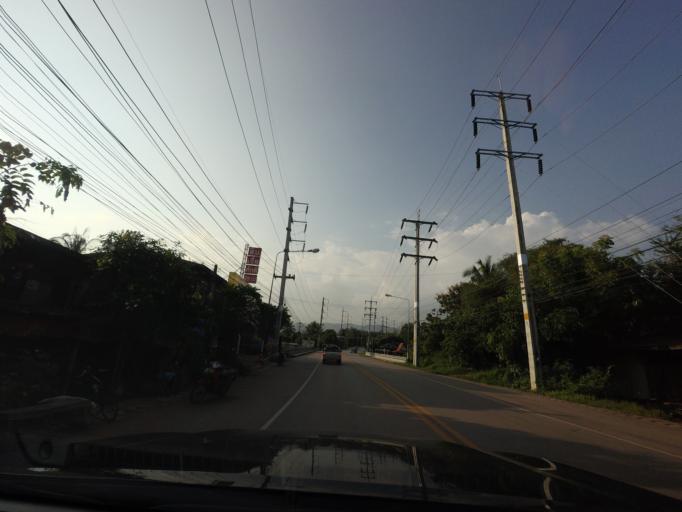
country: TH
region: Loei
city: Dan Sai
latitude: 17.2742
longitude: 101.1413
